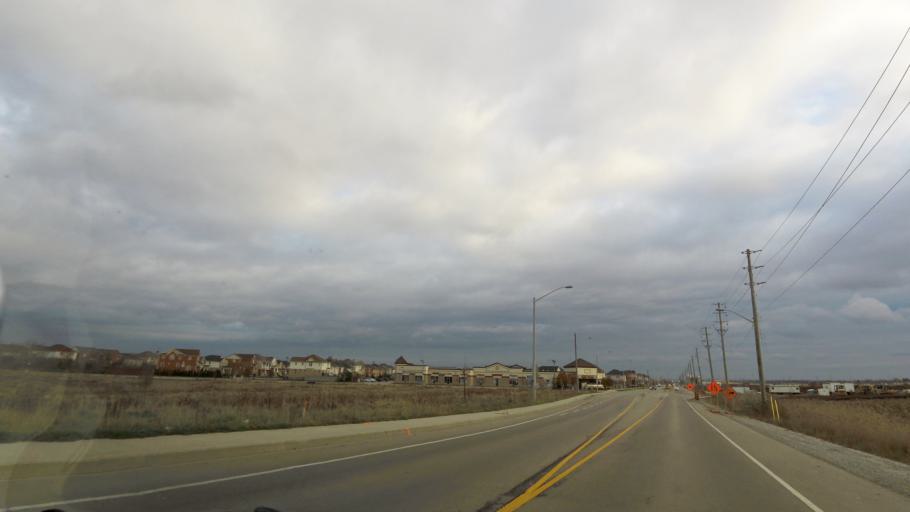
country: CA
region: Ontario
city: Burlington
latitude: 43.3974
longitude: -79.8311
